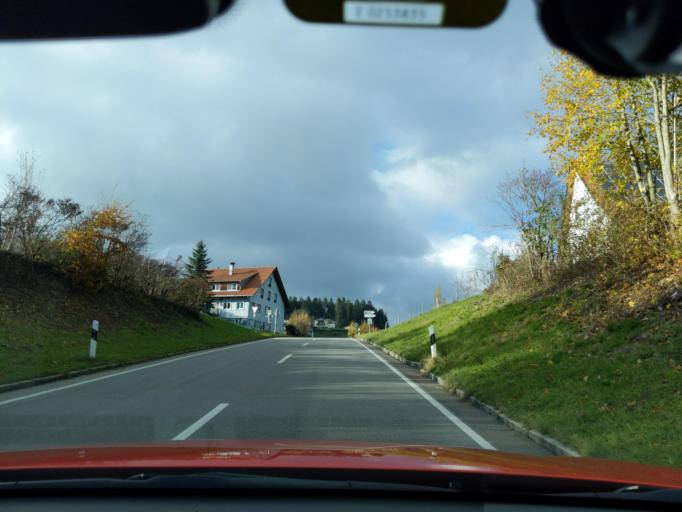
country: DE
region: Bavaria
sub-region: Swabia
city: Scheidegg
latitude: 47.5720
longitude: 9.8479
